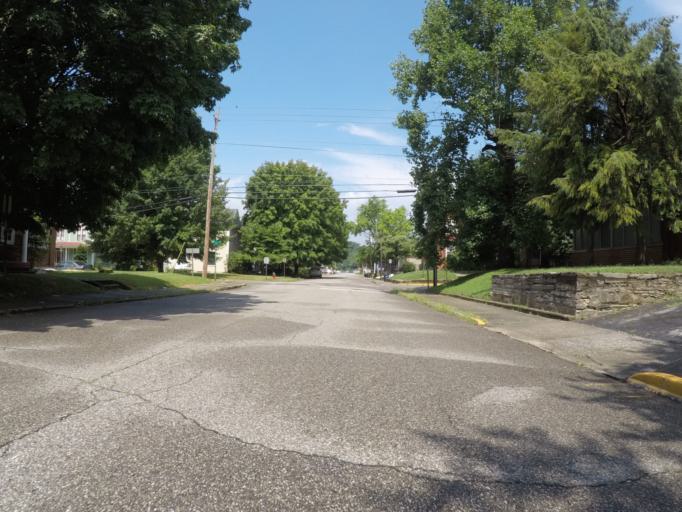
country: US
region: Kentucky
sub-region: Boyd County
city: Ashland
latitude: 38.4760
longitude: -82.6445
